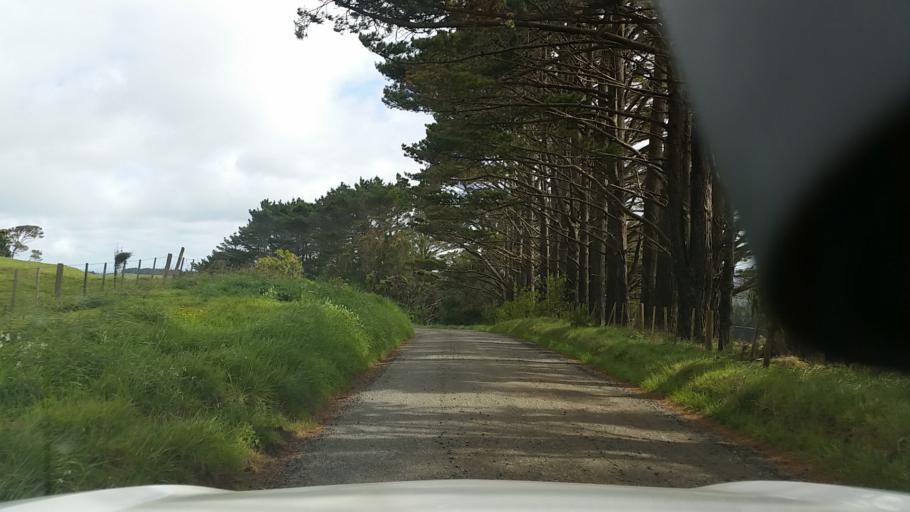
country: NZ
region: Auckland
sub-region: Auckland
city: Muriwai Beach
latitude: -36.8505
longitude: 174.4837
